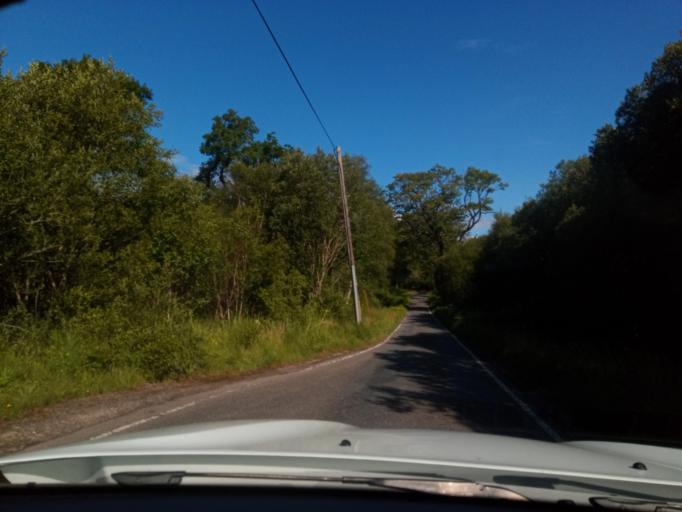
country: GB
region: Scotland
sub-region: Argyll and Bute
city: Isle Of Mull
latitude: 56.6961
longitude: -5.6845
